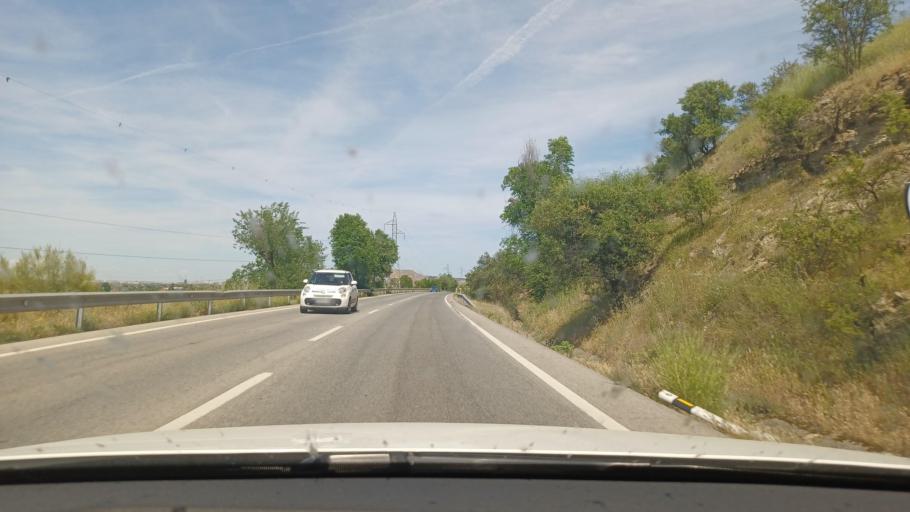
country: ES
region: Madrid
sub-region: Provincia de Madrid
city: Mejorada del Campo
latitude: 40.4190
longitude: -3.4693
